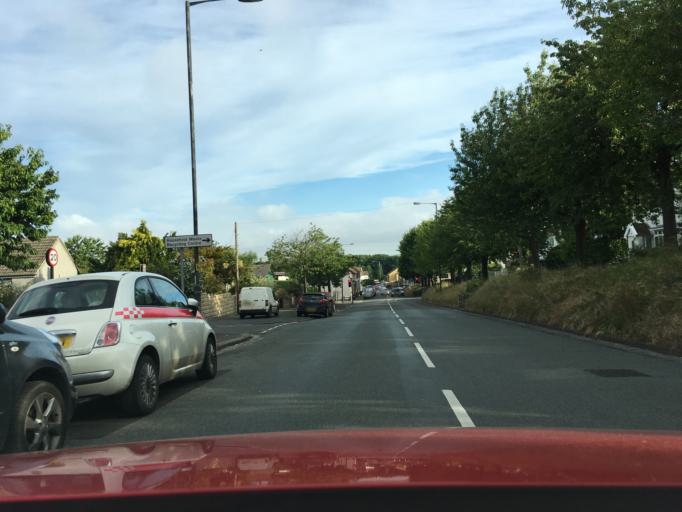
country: GB
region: England
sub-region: North Somerset
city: Easton-in-Gordano
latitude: 51.4932
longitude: -2.6812
